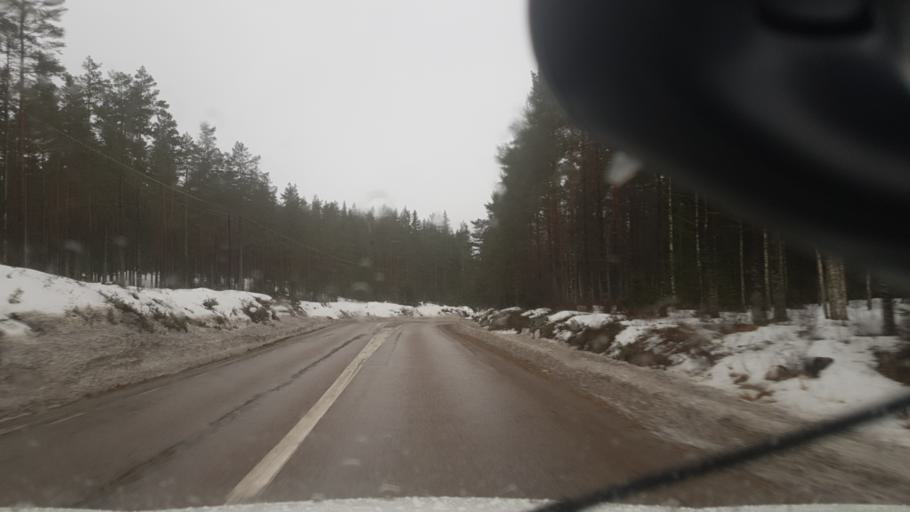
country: SE
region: Vaermland
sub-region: Arjangs Kommun
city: Arjaeng
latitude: 59.5622
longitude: 12.1829
